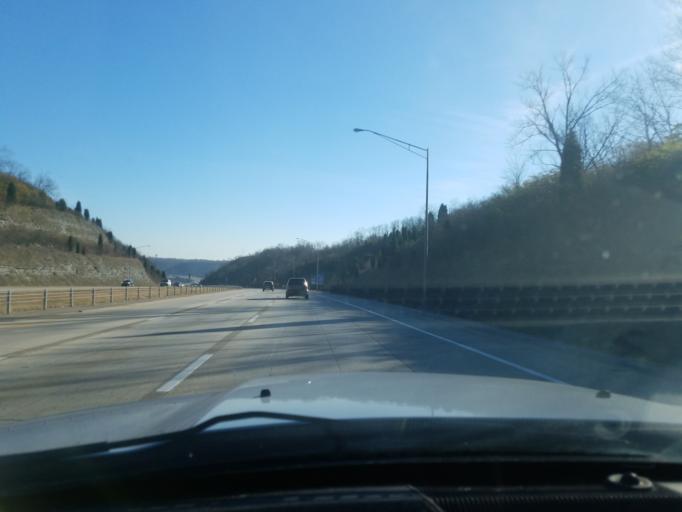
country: US
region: Kentucky
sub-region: Kenton County
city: Taylor Mill
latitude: 39.0216
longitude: -84.5101
